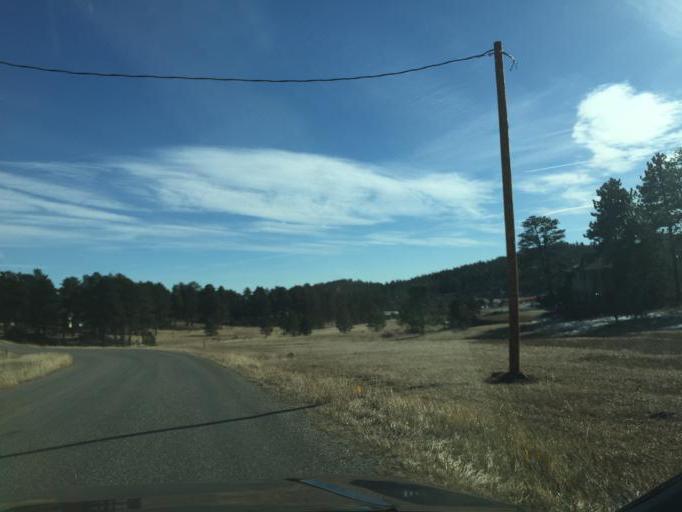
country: US
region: Colorado
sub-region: Jefferson County
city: Evergreen
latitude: 39.4425
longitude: -105.4580
